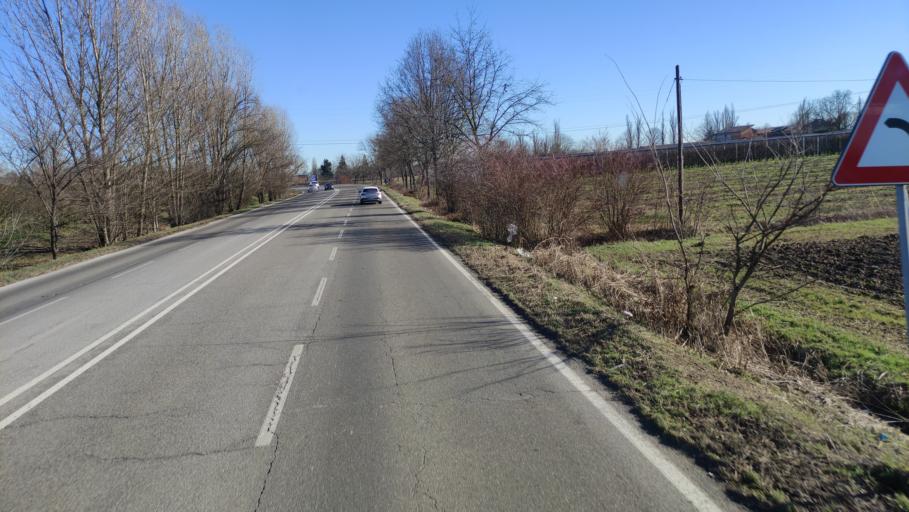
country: IT
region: Emilia-Romagna
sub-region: Provincia di Reggio Emilia
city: Correggio
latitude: 44.7604
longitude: 10.8033
